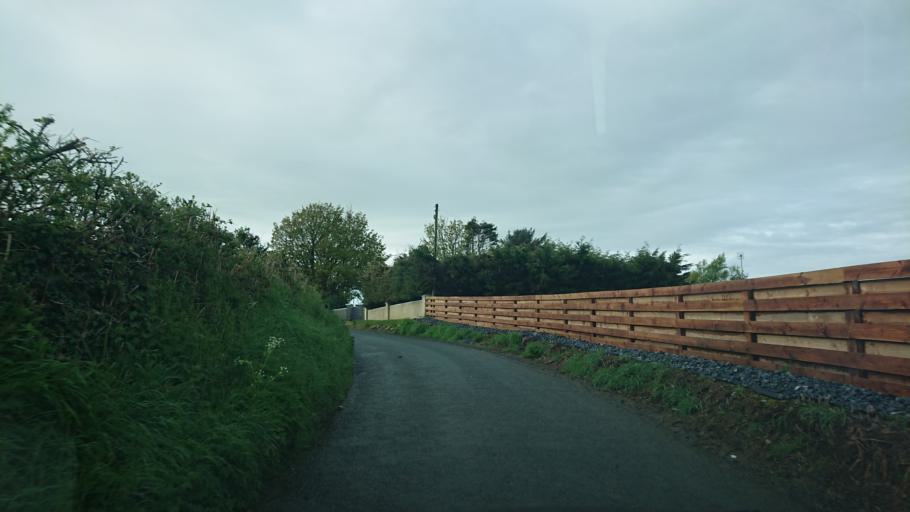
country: IE
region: Munster
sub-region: Waterford
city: Waterford
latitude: 52.2226
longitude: -7.1313
